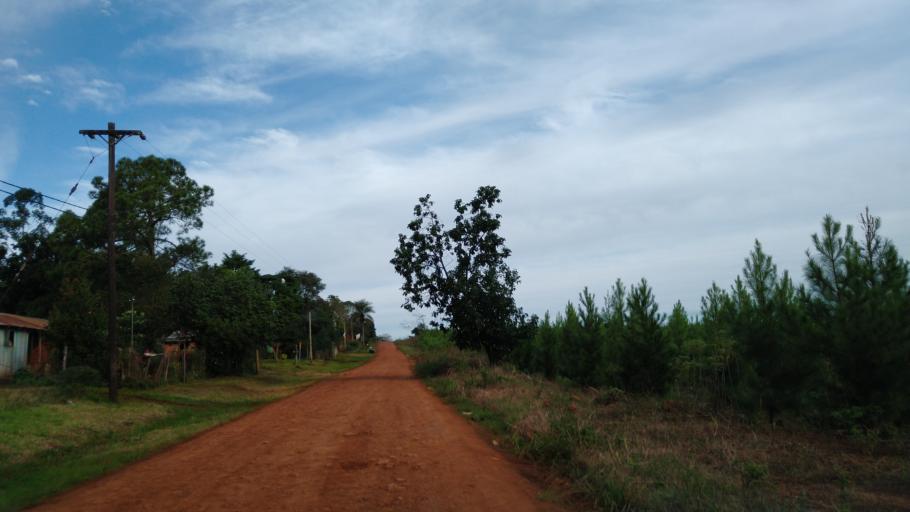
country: AR
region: Misiones
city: Capiovi
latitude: -26.9417
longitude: -55.0965
